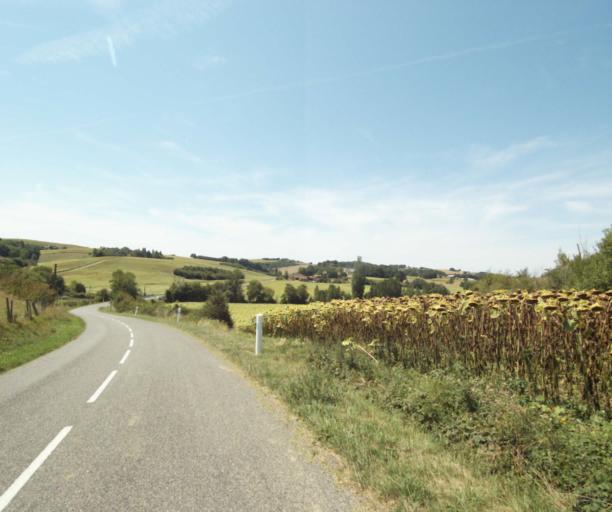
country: FR
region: Midi-Pyrenees
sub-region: Departement de l'Ariege
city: Lezat-sur-Leze
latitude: 43.2727
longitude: 1.3047
